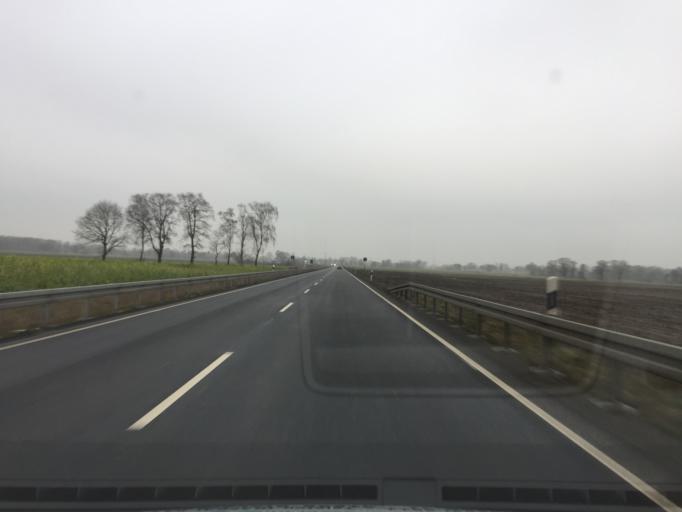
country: DE
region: Lower Saxony
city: Barenburg
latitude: 52.6087
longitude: 8.8127
